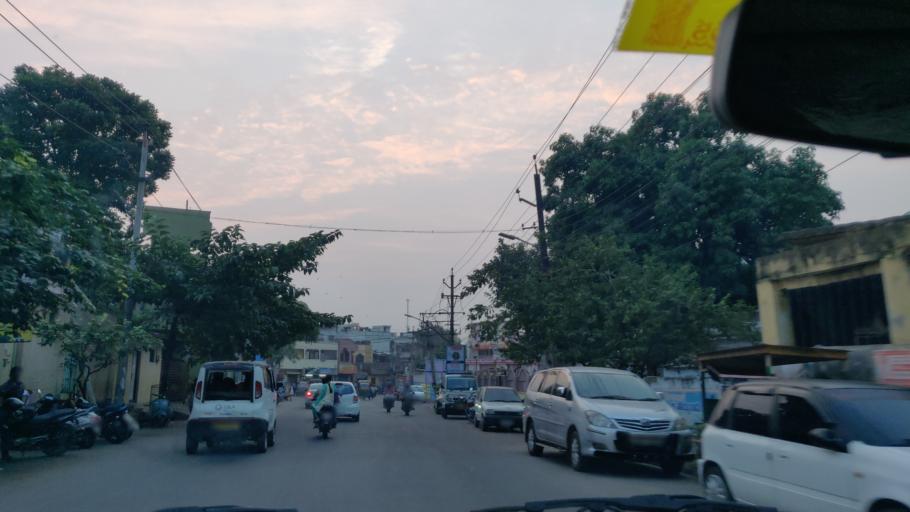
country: IN
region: Andhra Pradesh
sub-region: Krishna
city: Vijayawada
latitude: 16.5071
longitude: 80.6399
